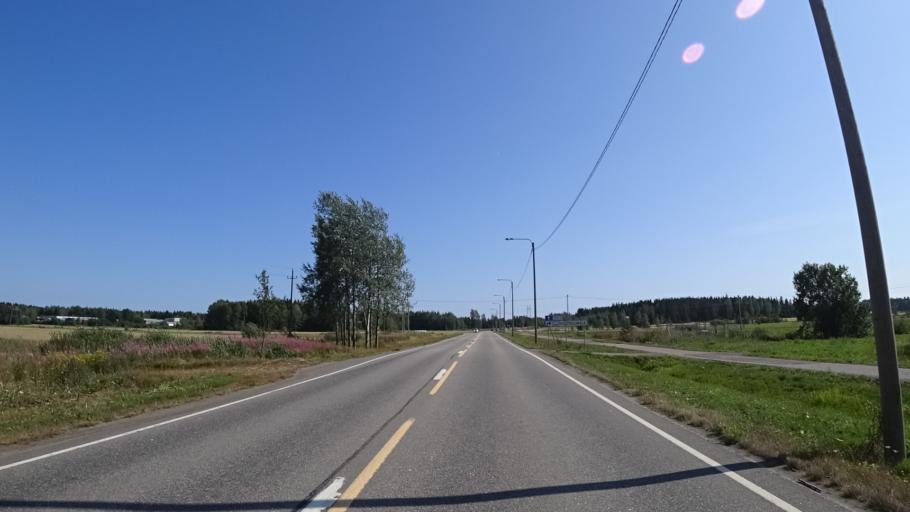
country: FI
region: Kymenlaakso
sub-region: Kotka-Hamina
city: Karhula
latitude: 60.5402
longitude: 26.9289
